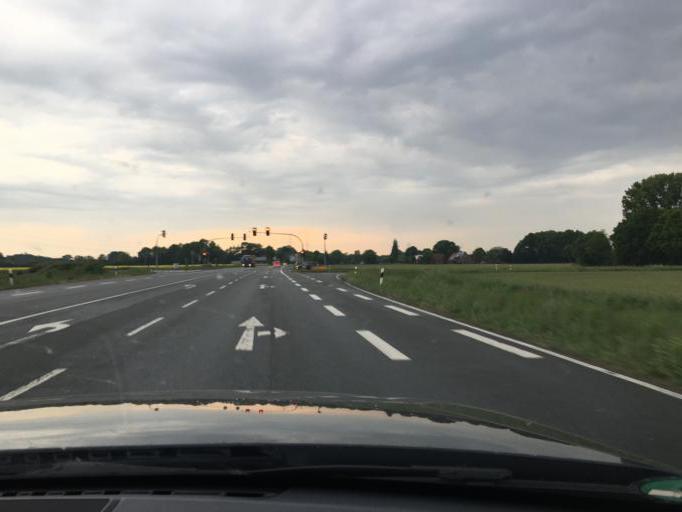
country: DE
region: North Rhine-Westphalia
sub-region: Regierungsbezirk Munster
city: Greven
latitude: 52.1273
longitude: 7.5835
